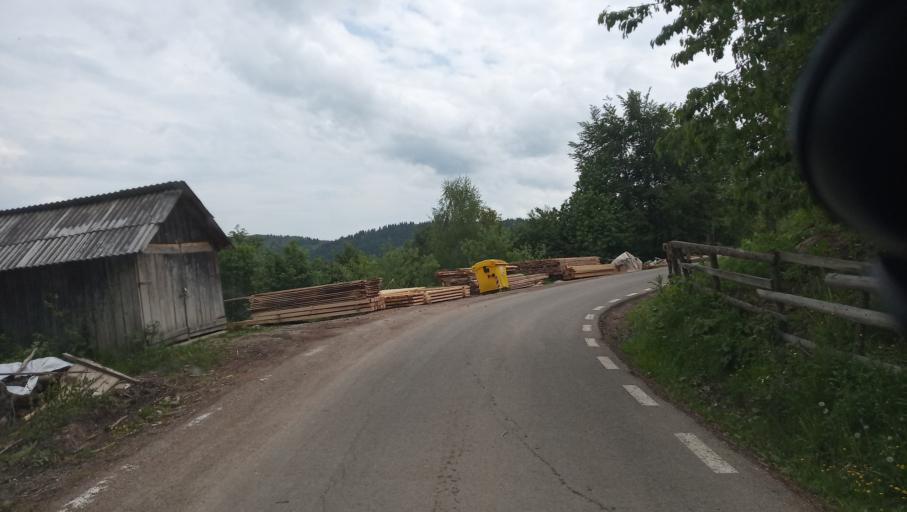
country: RO
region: Alba
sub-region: Comuna Horea
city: Horea
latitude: 46.5061
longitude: 22.8951
